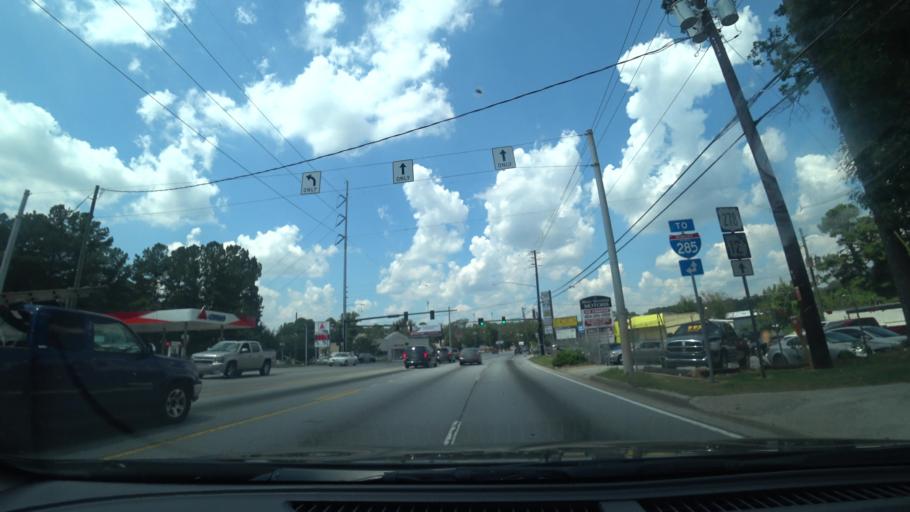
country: US
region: Georgia
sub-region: DeKalb County
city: Belvedere Park
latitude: 33.7365
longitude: -84.2164
